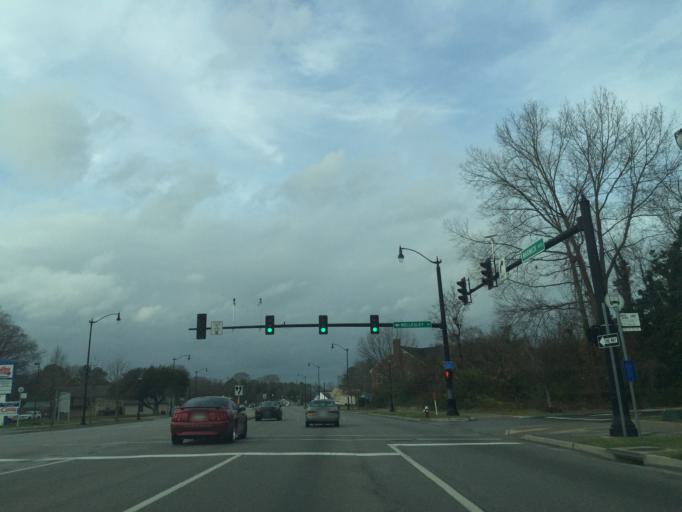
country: US
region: Virginia
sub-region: City of Newport News
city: Newport News
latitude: 37.0771
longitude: -76.4950
